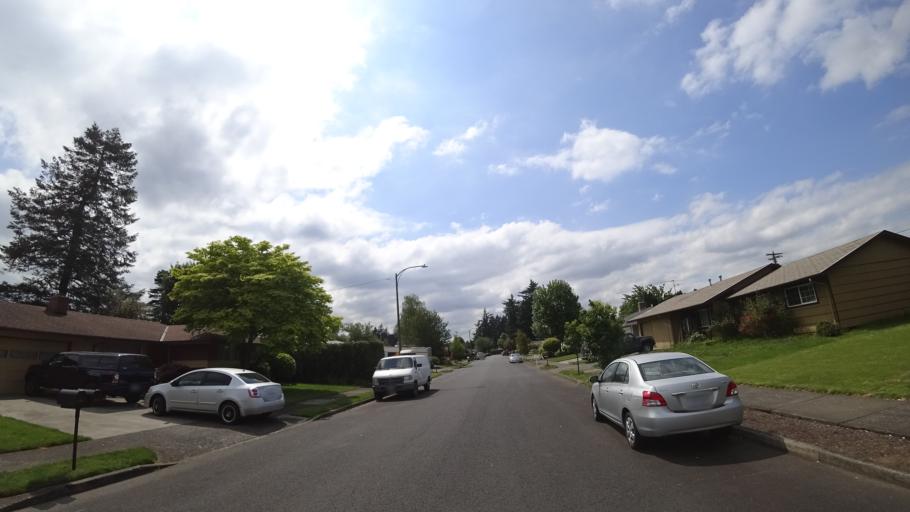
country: US
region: Oregon
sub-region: Multnomah County
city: Fairview
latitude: 45.5151
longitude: -122.4868
